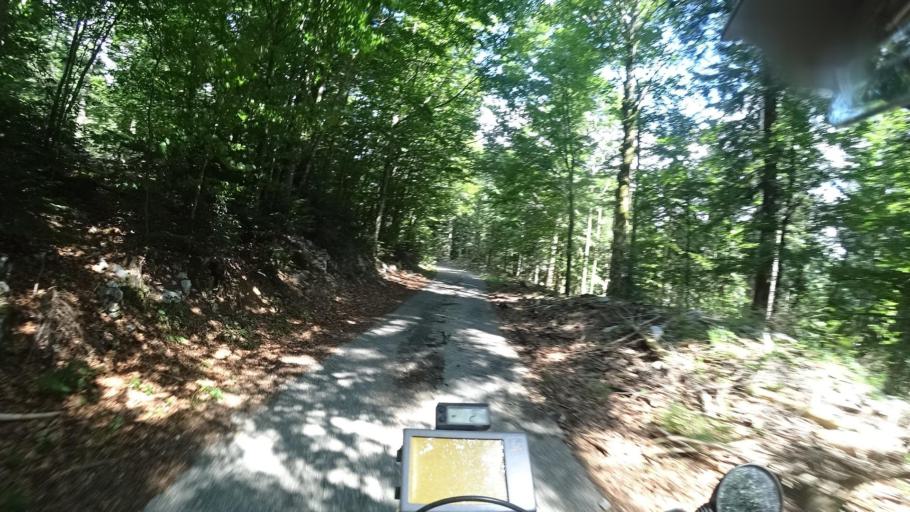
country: HR
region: Licko-Senjska
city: Brinje
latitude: 45.1066
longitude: 15.0298
